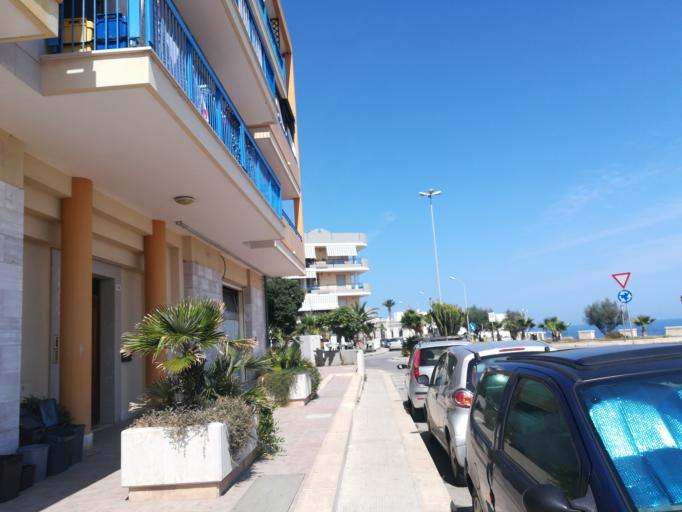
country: IT
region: Apulia
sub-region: Provincia di Bari
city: Polignano a Mare
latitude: 40.9926
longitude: 17.2297
